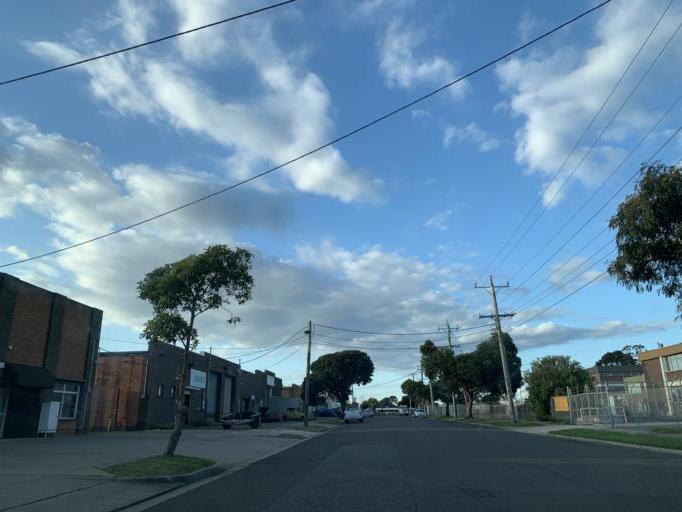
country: AU
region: Victoria
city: Heatherton
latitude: -37.9784
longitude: 145.0884
